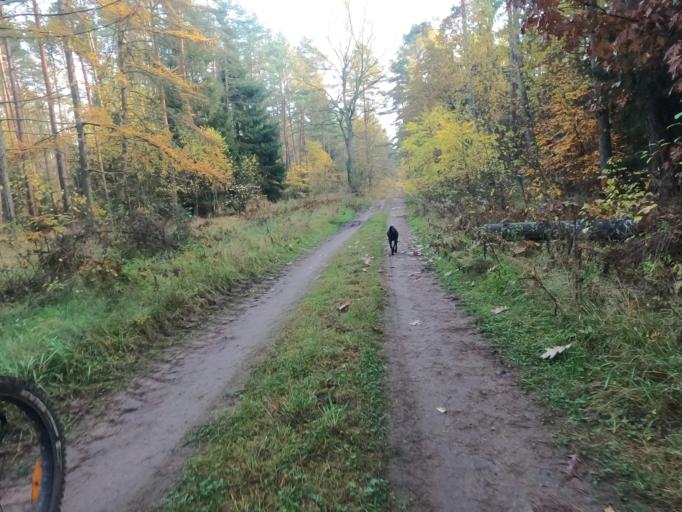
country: PL
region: West Pomeranian Voivodeship
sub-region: Powiat szczecinecki
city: Lubowo
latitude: 53.5752
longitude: 16.4064
